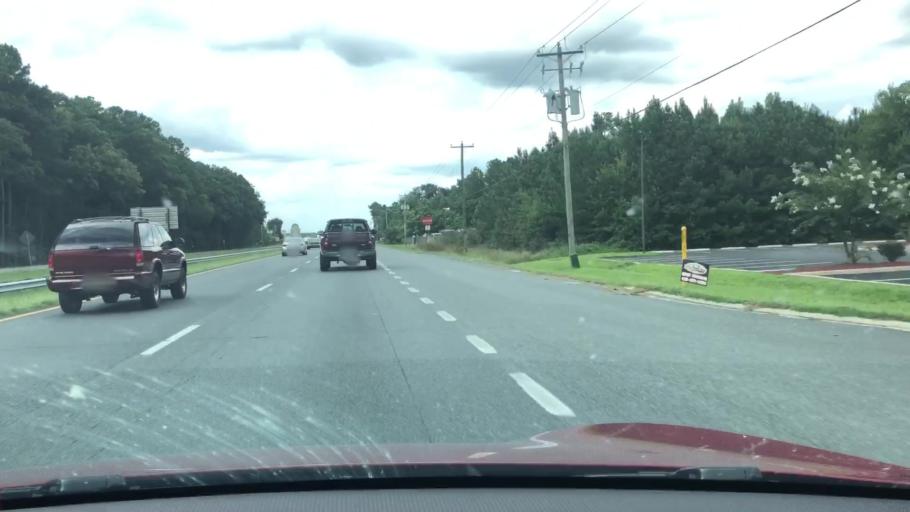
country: US
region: Delaware
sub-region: Sussex County
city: Delmar
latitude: 38.4481
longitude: -75.5596
